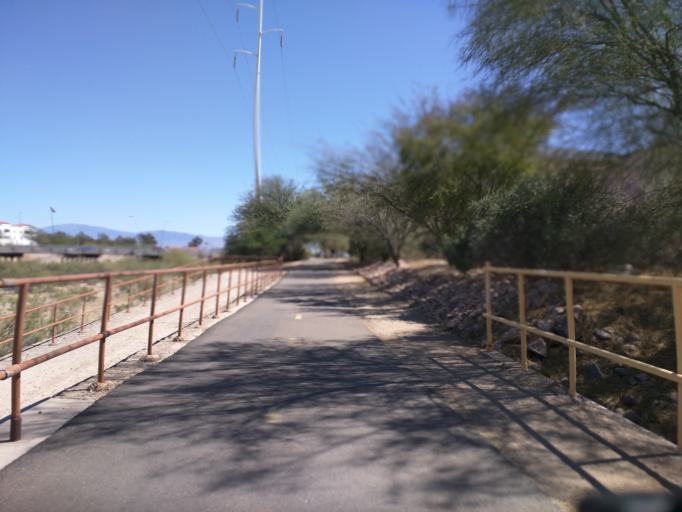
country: US
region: Arizona
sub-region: Pima County
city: Catalina Foothills
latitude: 32.2849
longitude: -110.9456
